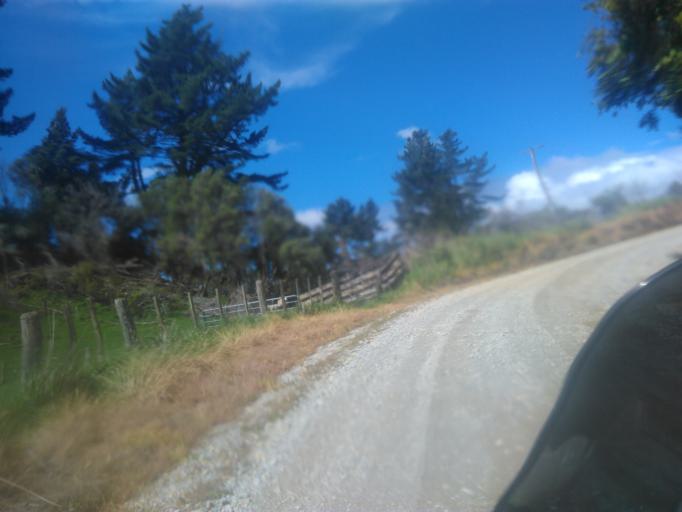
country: NZ
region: Hawke's Bay
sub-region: Wairoa District
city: Wairoa
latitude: -38.7768
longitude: 177.6117
